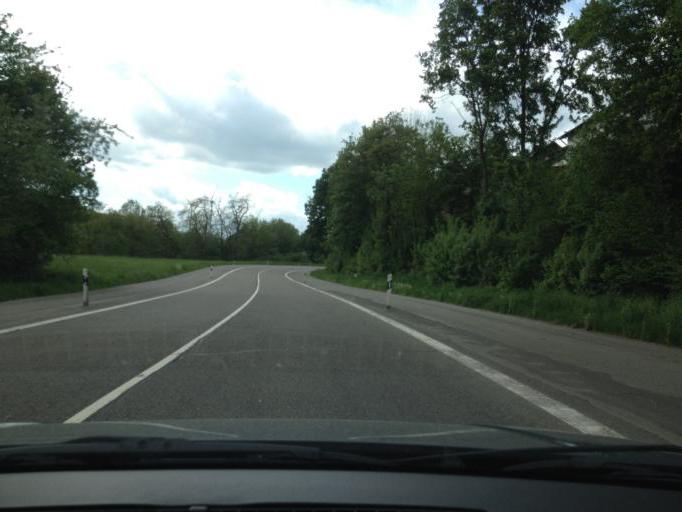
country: DE
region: Saarland
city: Ottweiler
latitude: 49.3792
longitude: 7.1767
